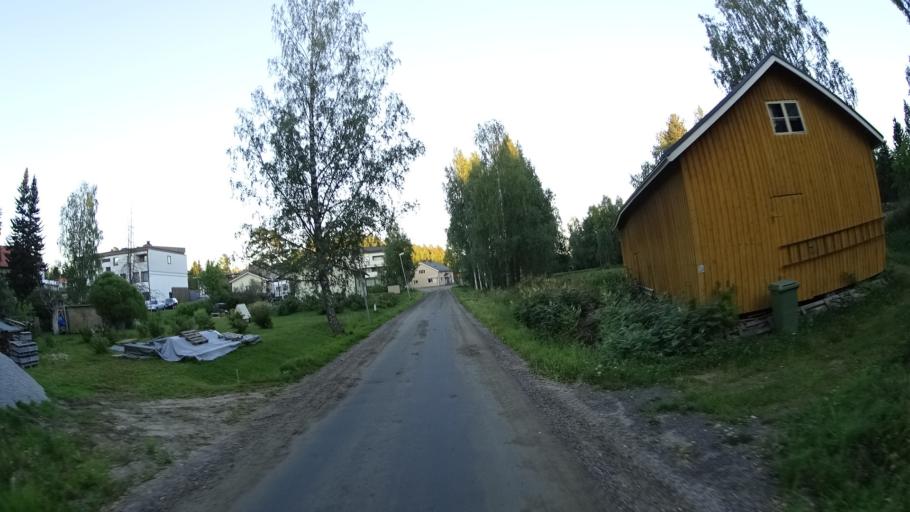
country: FI
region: Central Finland
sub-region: Jyvaeskylae
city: Petaejaevesi
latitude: 62.2556
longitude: 25.1808
